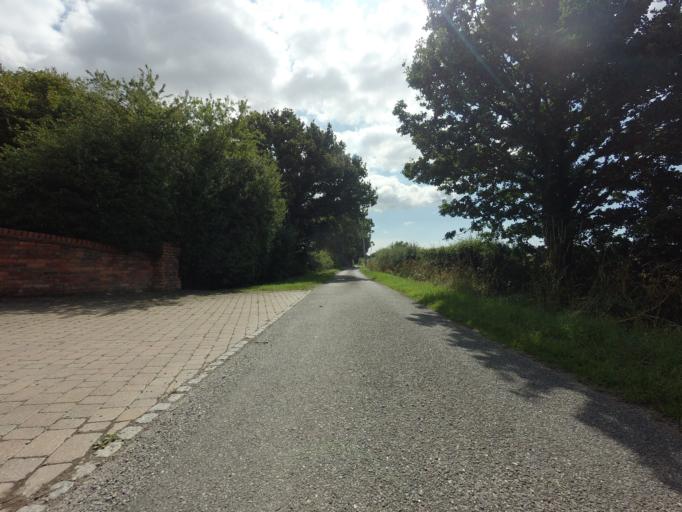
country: GB
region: England
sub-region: Kent
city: Stone
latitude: 51.0482
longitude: 0.7737
